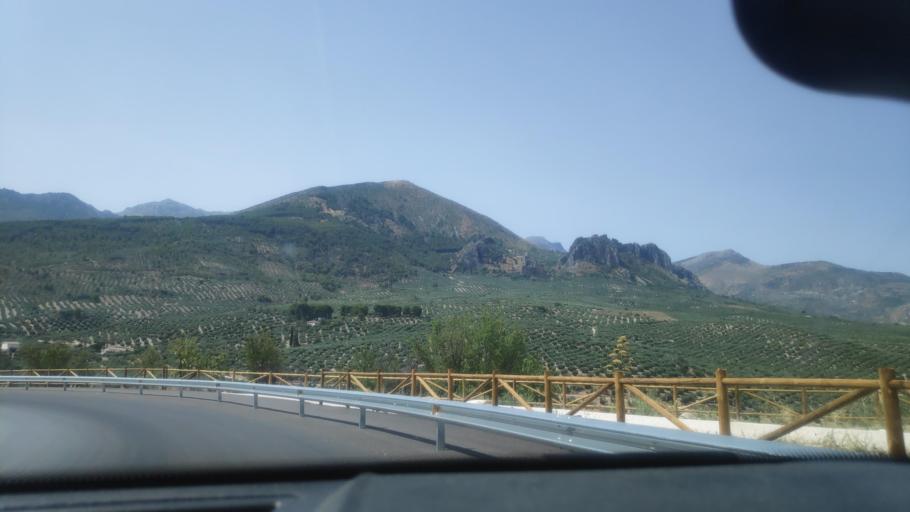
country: ES
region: Andalusia
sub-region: Provincia de Jaen
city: Jimena
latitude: 37.8070
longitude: -3.4153
